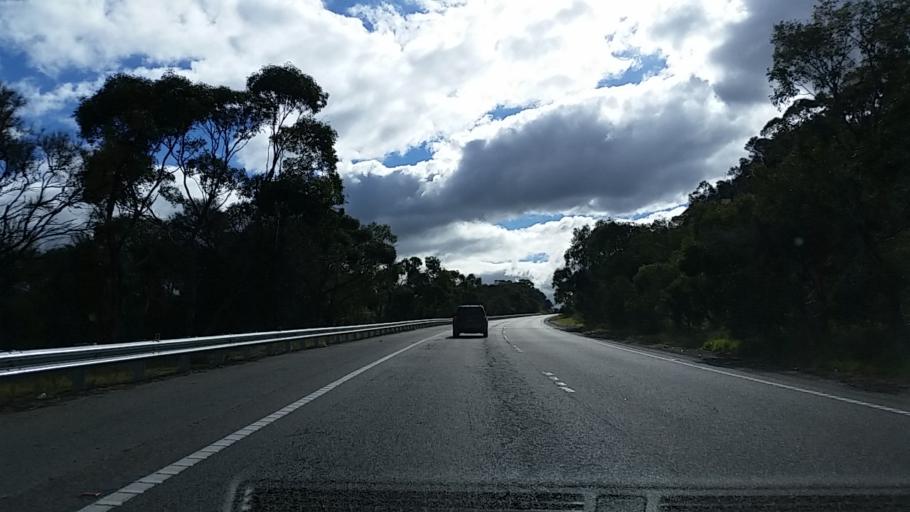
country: AU
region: South Australia
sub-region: Mount Barker
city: Callington
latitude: -35.1074
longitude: 138.9739
